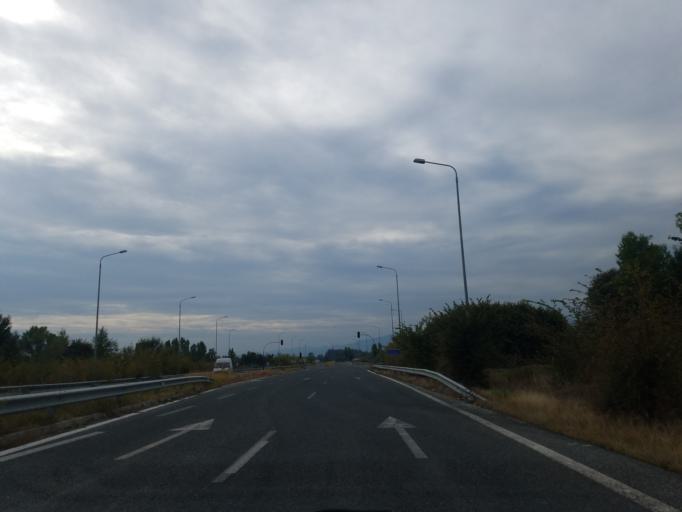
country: GR
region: Thessaly
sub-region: Trikala
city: Pyrgetos
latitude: 39.5421
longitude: 21.7355
